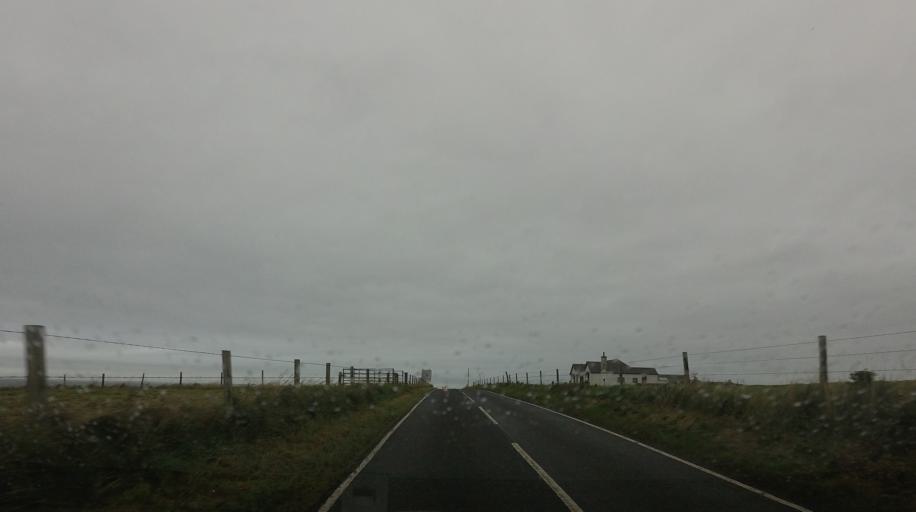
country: GB
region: Scotland
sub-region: Orkney Islands
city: Stromness
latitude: 59.1298
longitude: -3.3030
